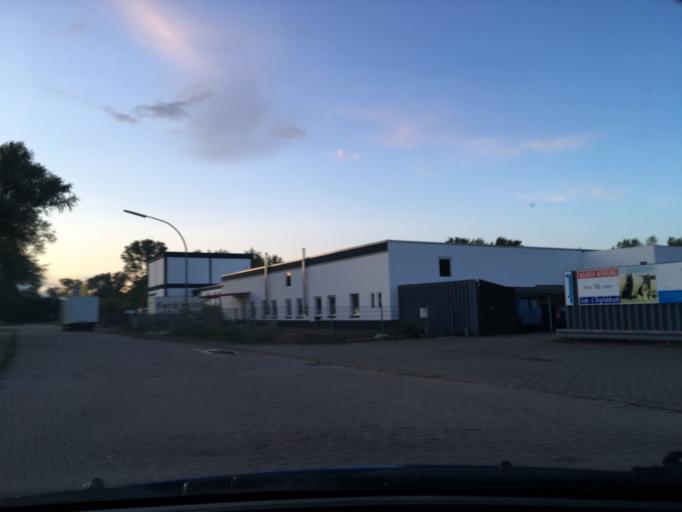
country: DE
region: Schleswig-Holstein
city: Lanze
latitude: 53.3713
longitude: 10.5872
